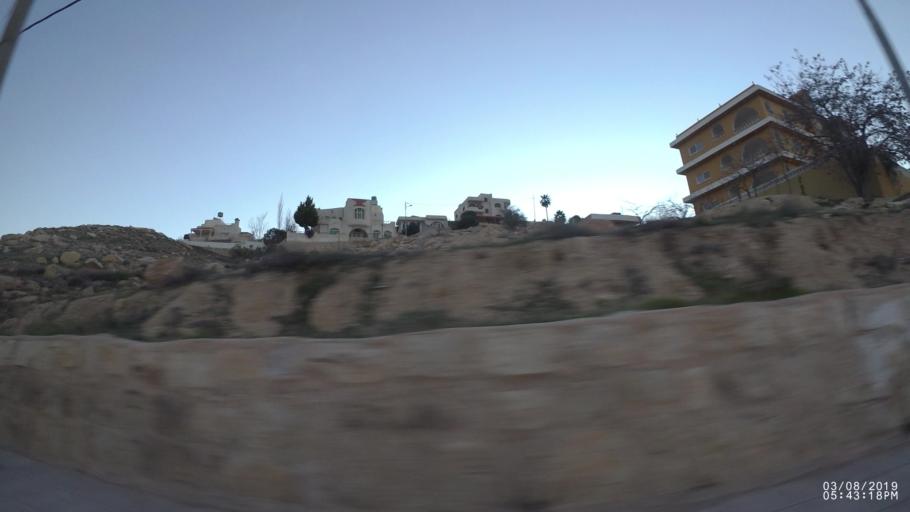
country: JO
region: Ma'an
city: Petra
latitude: 30.3147
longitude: 35.4771
